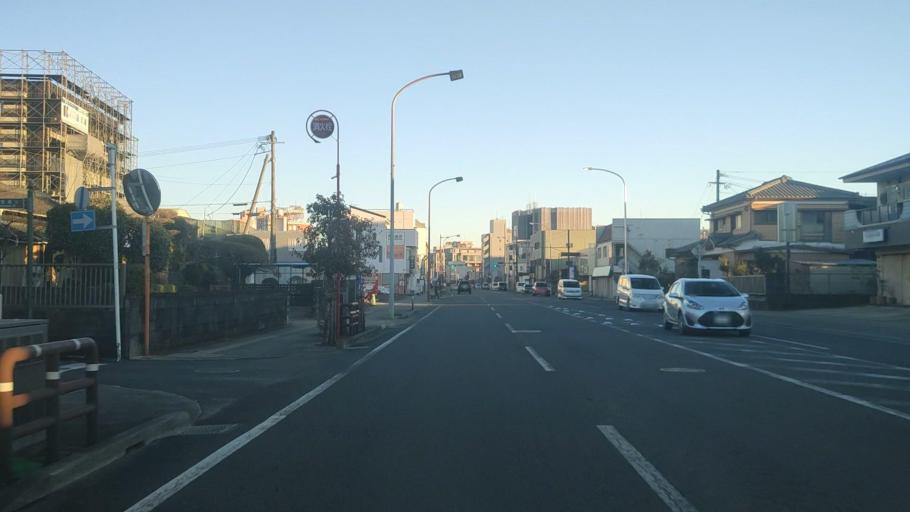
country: JP
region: Miyazaki
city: Miyazaki-shi
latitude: 31.9118
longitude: 131.4149
